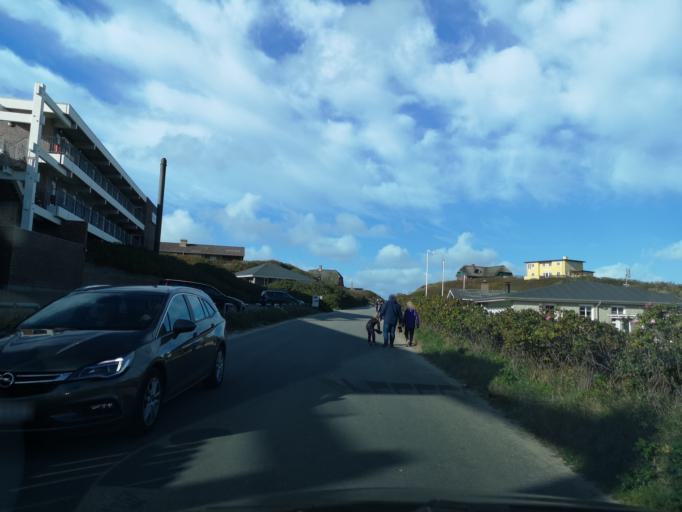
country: DK
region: South Denmark
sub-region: Varde Kommune
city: Oksbol
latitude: 55.7410
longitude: 8.1774
